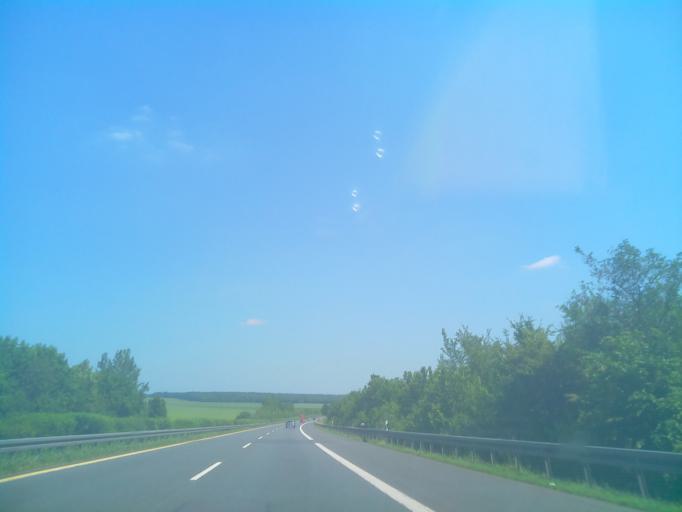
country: DE
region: Baden-Wuerttemberg
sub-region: Regierungsbezirk Stuttgart
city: Grossrinderfeld
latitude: 49.6486
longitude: 9.7378
